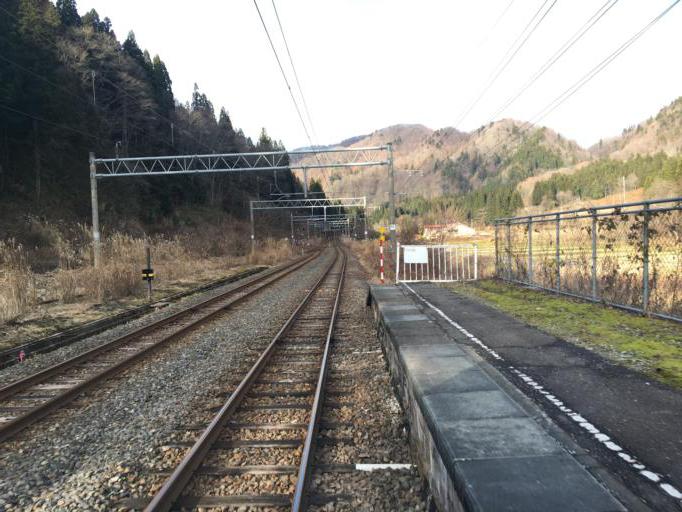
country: JP
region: Akita
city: Yuzawa
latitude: 38.9937
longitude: 140.3614
